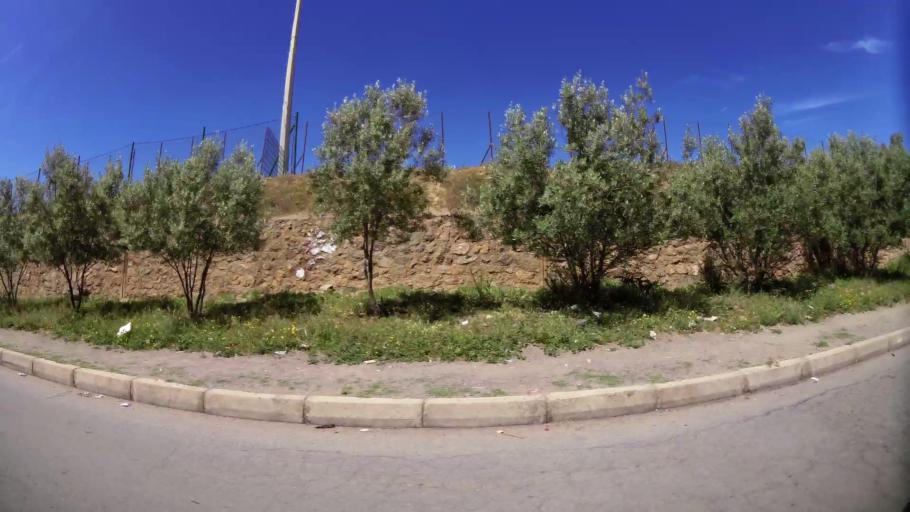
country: MA
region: Oriental
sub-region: Oujda-Angad
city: Oujda
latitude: 34.6627
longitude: -1.9345
